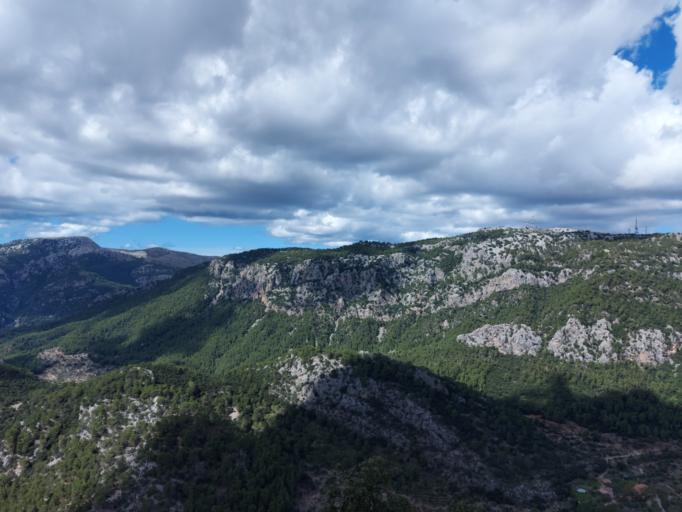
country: ES
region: Balearic Islands
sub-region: Illes Balears
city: Bunyola
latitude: 39.7166
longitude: 2.7228
